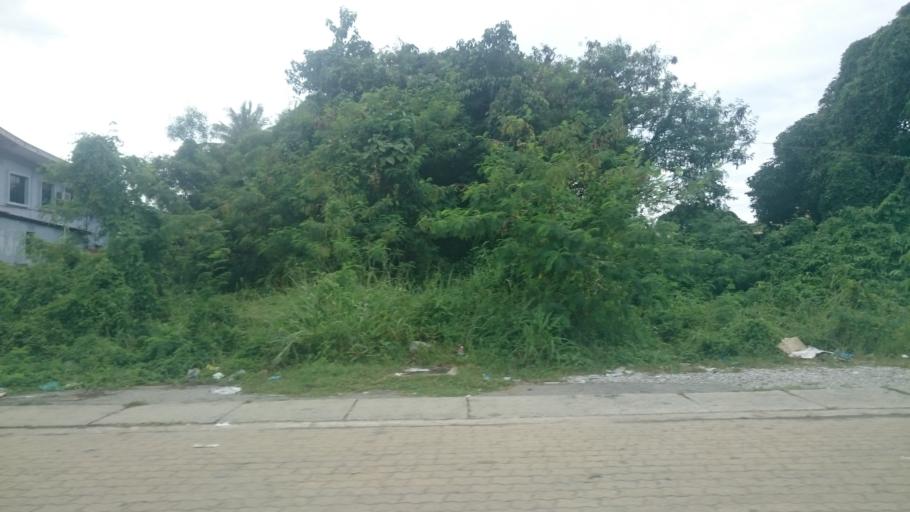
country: BN
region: Brunei and Muara
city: Bandar Seri Begawan
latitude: 4.9447
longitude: 114.8411
